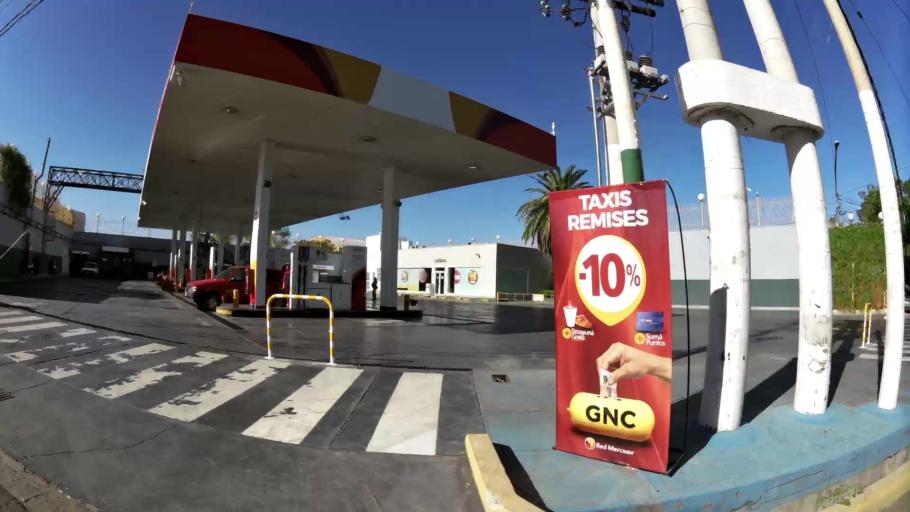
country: AR
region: Mendoza
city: Mendoza
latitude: -32.9014
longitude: -68.8151
